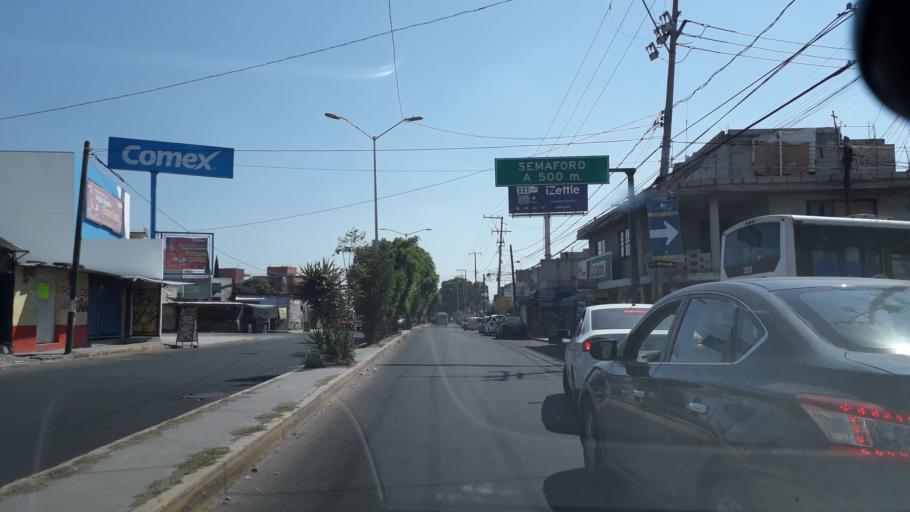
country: MX
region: Puebla
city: Puebla
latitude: 18.9868
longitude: -98.2161
